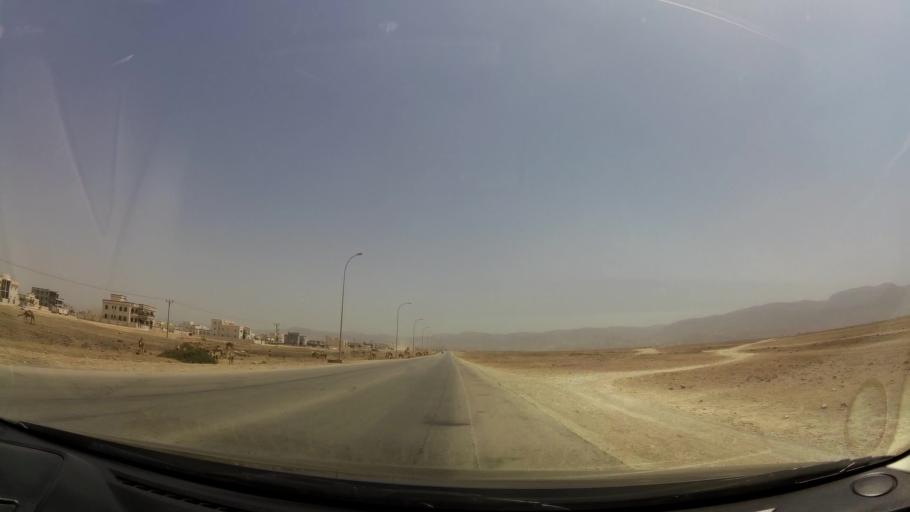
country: OM
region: Zufar
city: Salalah
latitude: 17.0692
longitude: 54.2172
